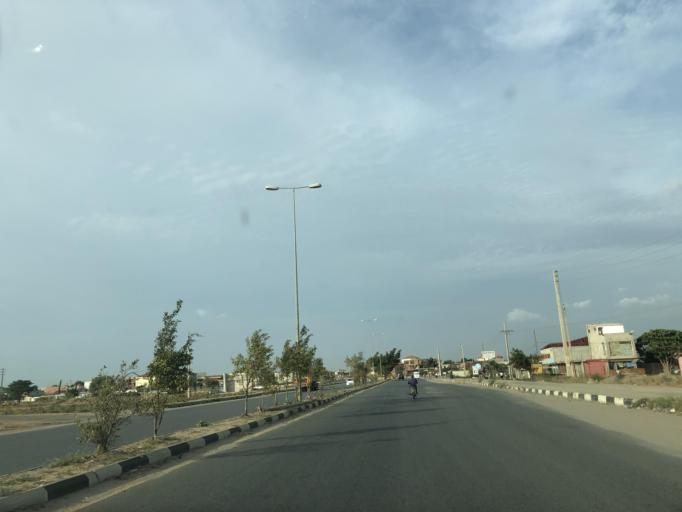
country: AO
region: Luanda
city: Luanda
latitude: -8.9315
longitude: 13.3017
